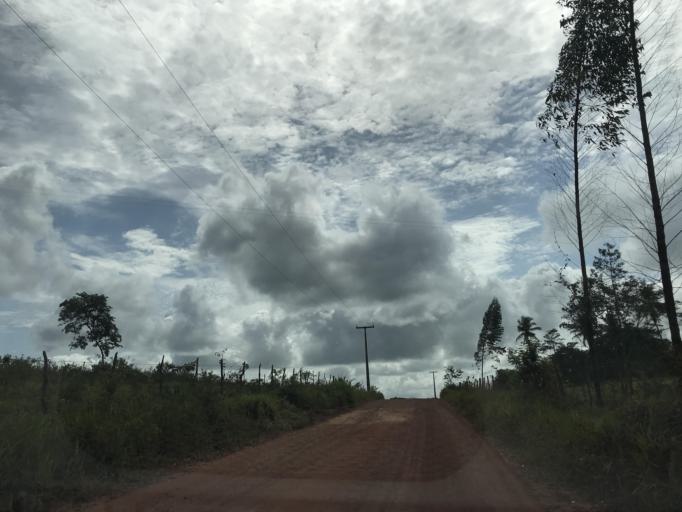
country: BR
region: Bahia
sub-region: Entre Rios
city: Entre Rios
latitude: -12.1667
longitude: -38.1564
